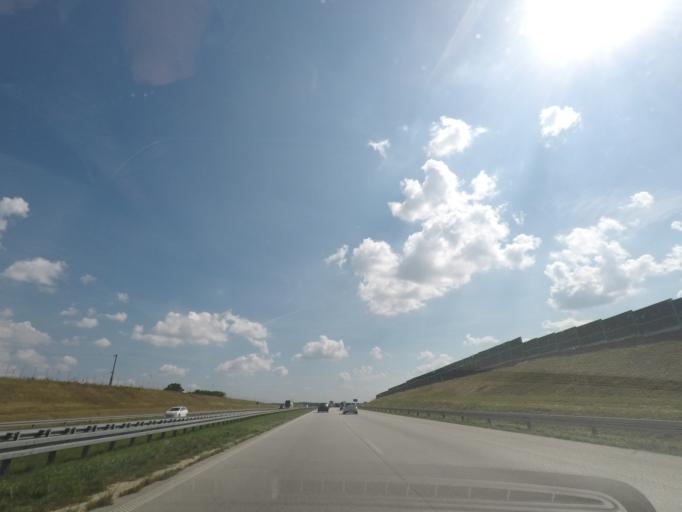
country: PL
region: Lodz Voivodeship
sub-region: Powiat zgierski
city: Strykow
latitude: 51.8552
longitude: 19.6596
